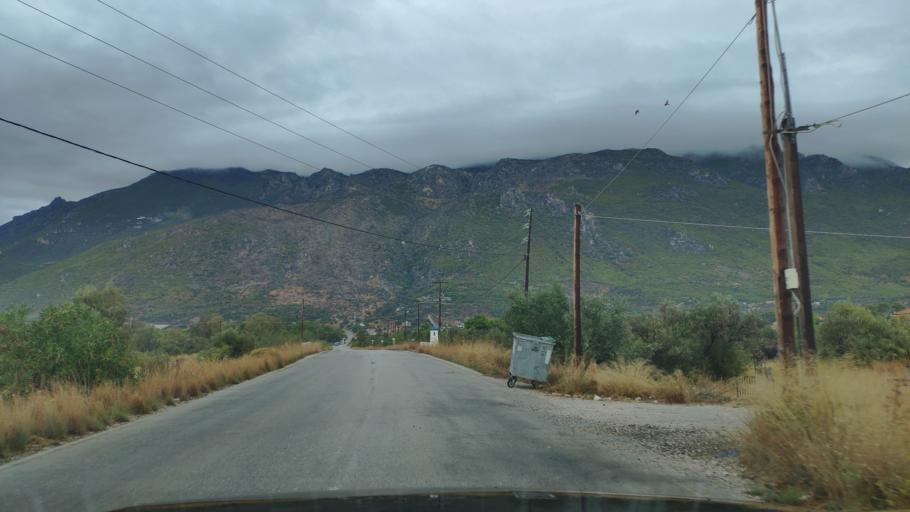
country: GR
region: Peloponnese
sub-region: Nomos Korinthias
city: Loutraki
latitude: 37.9681
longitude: 22.9875
